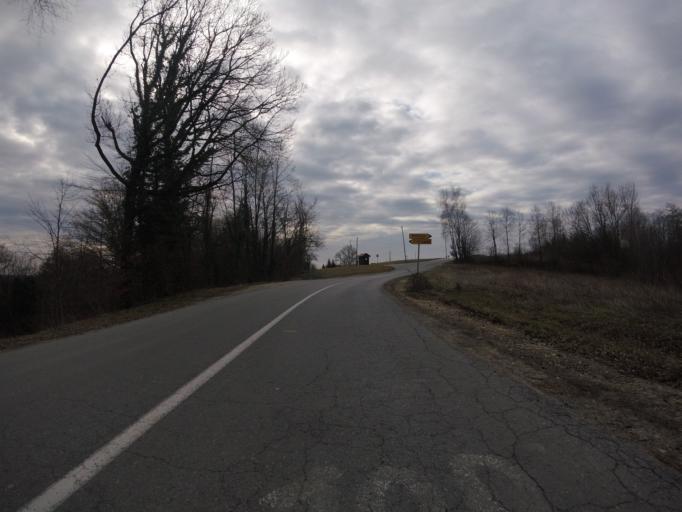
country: HR
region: Zagrebacka
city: Mraclin
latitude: 45.5412
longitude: 16.0615
